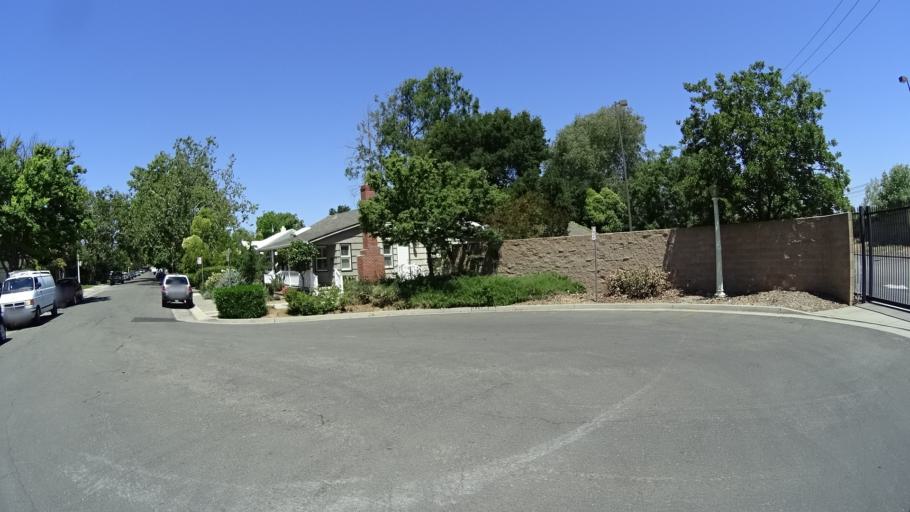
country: US
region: California
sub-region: Sacramento County
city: Sacramento
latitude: 38.5460
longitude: -121.4870
